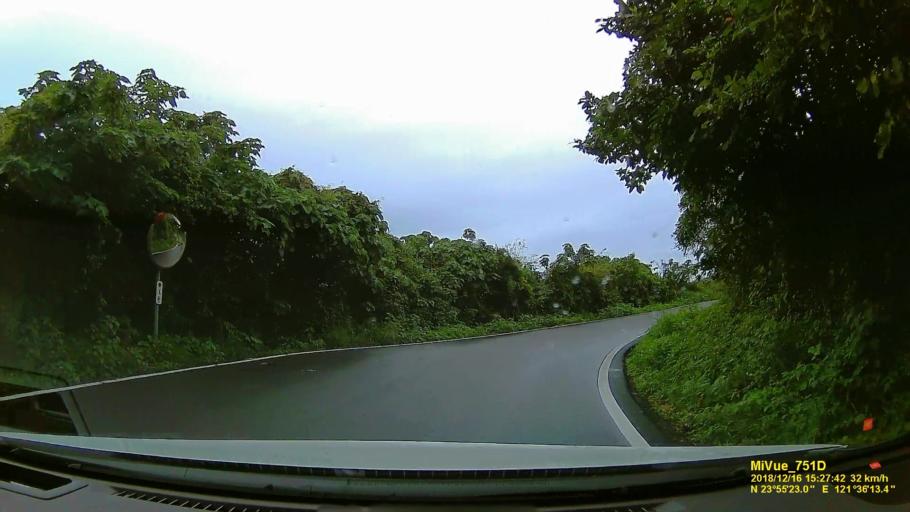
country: TW
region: Taiwan
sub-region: Hualien
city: Hualian
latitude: 23.9230
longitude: 121.6039
